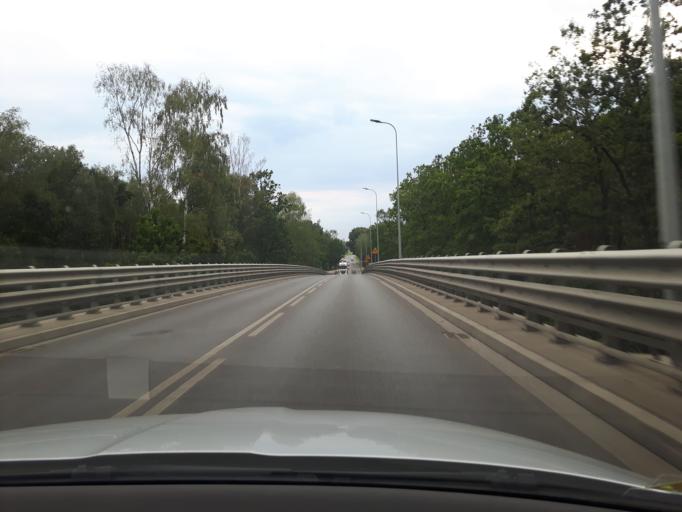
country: PL
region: Masovian Voivodeship
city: Zielonka
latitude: 52.2979
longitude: 21.1467
